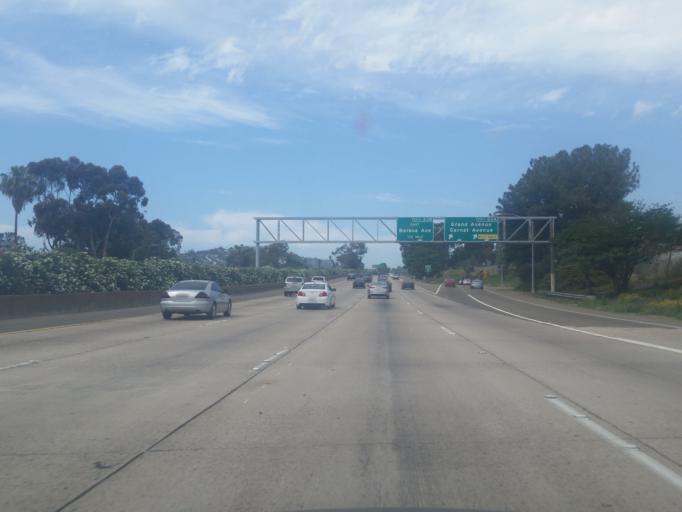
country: US
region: California
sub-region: San Diego County
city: La Jolla
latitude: 32.7962
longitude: -117.2090
